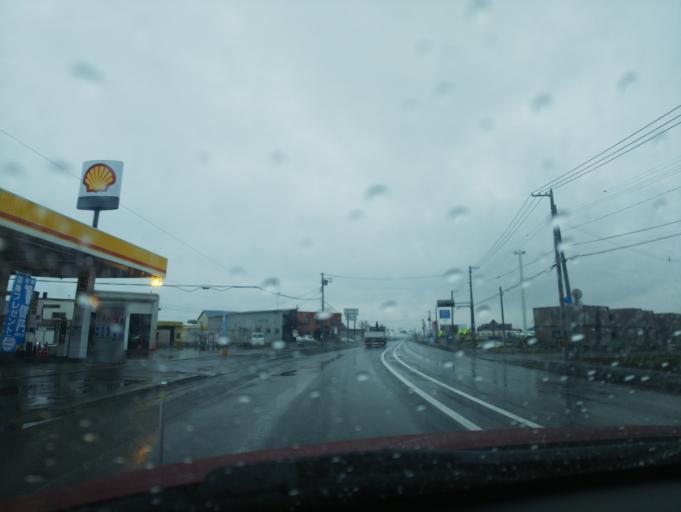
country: JP
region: Hokkaido
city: Nayoro
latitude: 44.1867
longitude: 142.3893
